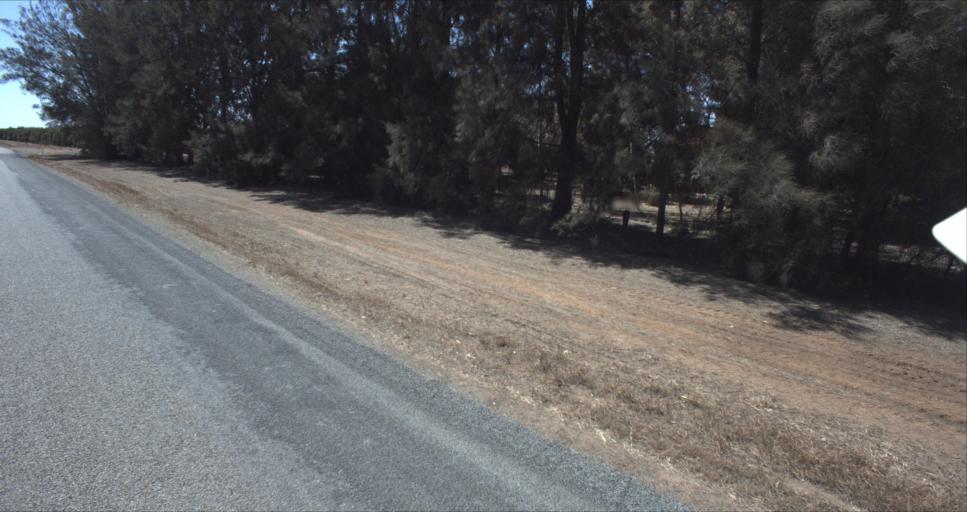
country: AU
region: New South Wales
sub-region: Leeton
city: Leeton
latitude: -34.5392
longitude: 146.3611
